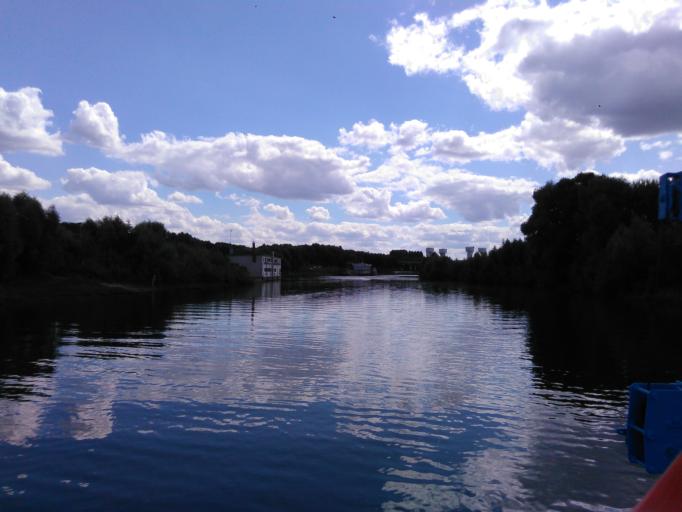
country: RU
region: Rjazan
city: Ryazan'
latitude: 54.6493
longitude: 39.7642
